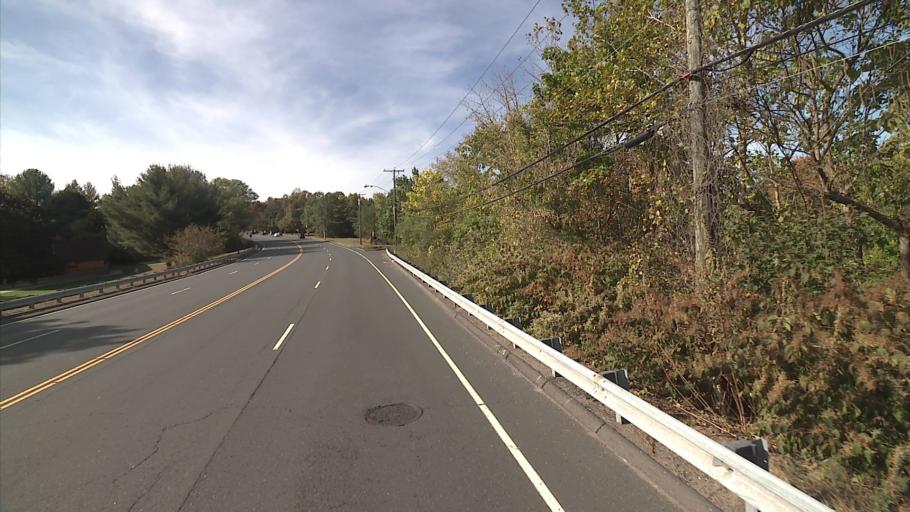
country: US
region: Connecticut
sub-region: Hartford County
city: Plainville
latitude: 41.7067
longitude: -72.8711
